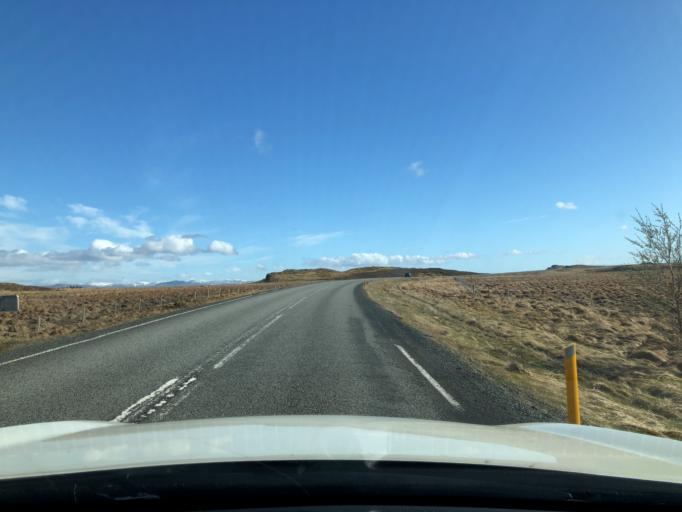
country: IS
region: West
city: Borgarnes
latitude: 64.5563
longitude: -21.7314
